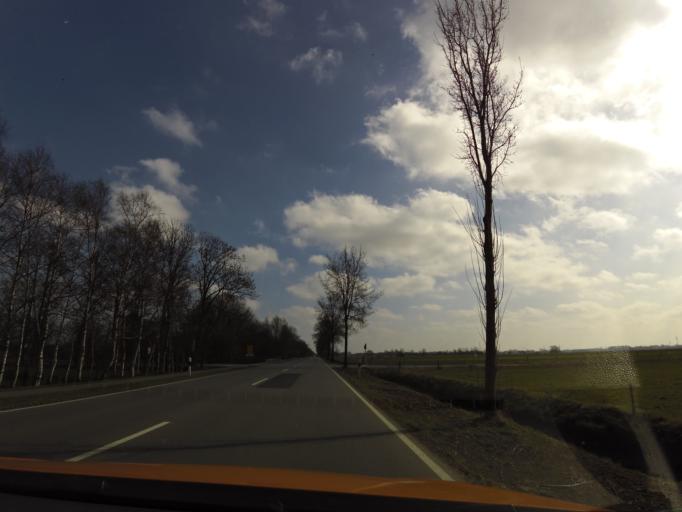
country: DE
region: Lower Saxony
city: Varel
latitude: 53.3866
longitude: 8.2137
